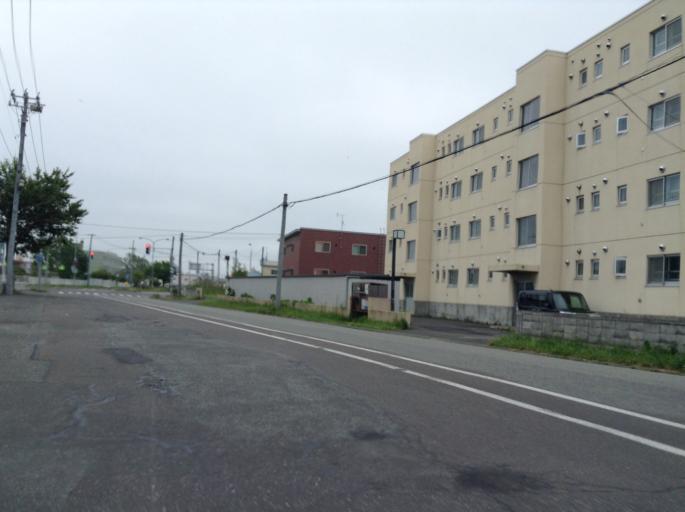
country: JP
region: Hokkaido
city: Wakkanai
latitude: 45.3950
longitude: 141.6917
